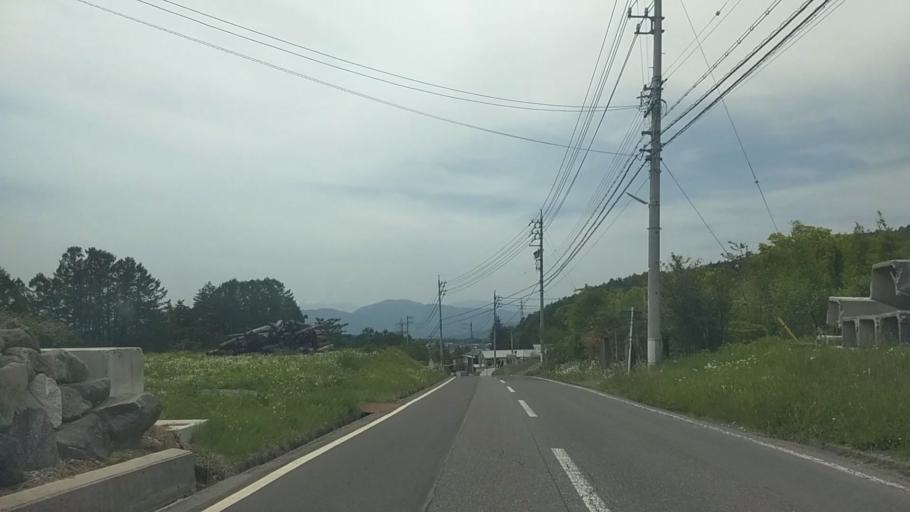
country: JP
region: Nagano
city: Chino
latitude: 36.0342
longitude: 138.2552
